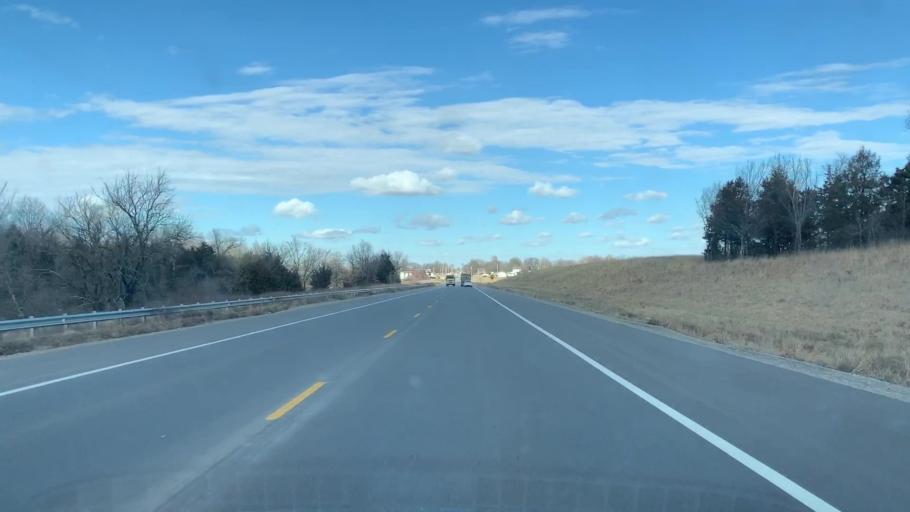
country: US
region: Kansas
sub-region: Crawford County
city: Pittsburg
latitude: 37.3332
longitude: -94.8321
